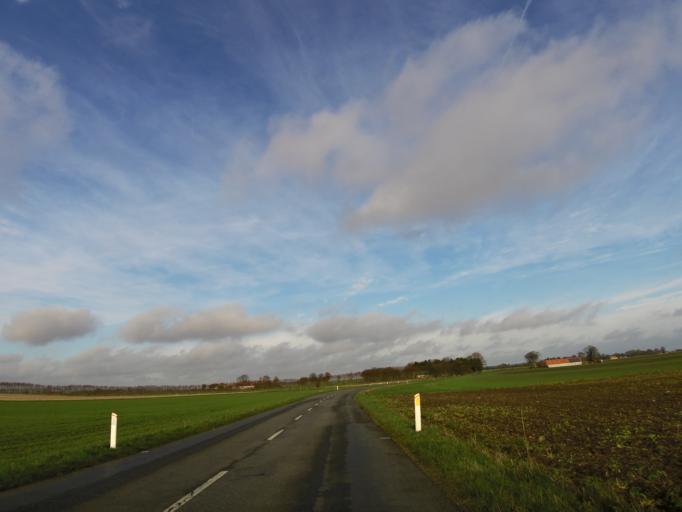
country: DK
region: Central Jutland
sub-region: Odder Kommune
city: Odder
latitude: 55.9442
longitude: 10.2349
